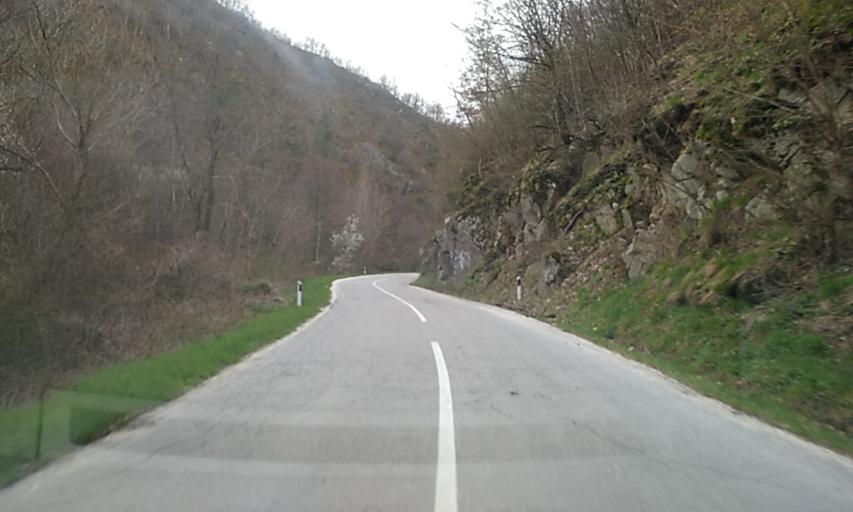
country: RS
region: Central Serbia
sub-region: Pcinjski Okrug
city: Bosilegrad
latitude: 42.5152
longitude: 22.4502
